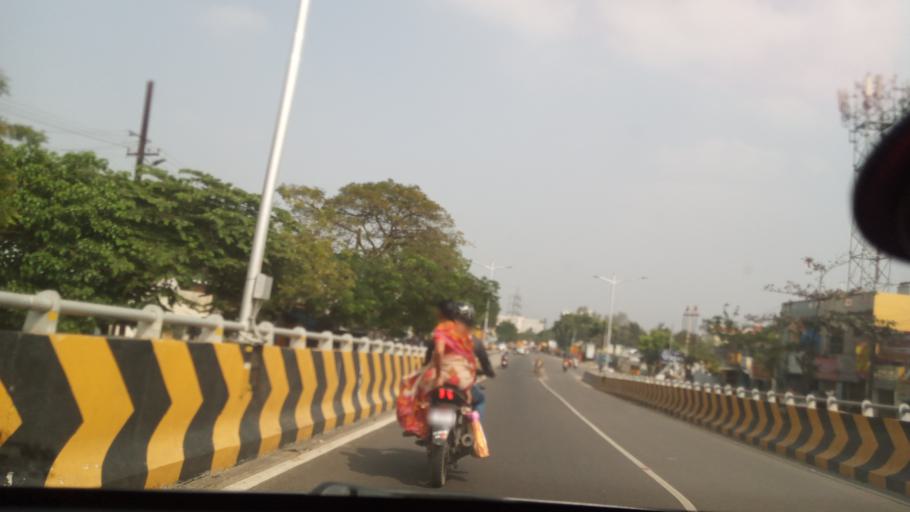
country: IN
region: Tamil Nadu
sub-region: Coimbatore
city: Coimbatore
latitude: 11.0213
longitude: 76.9811
